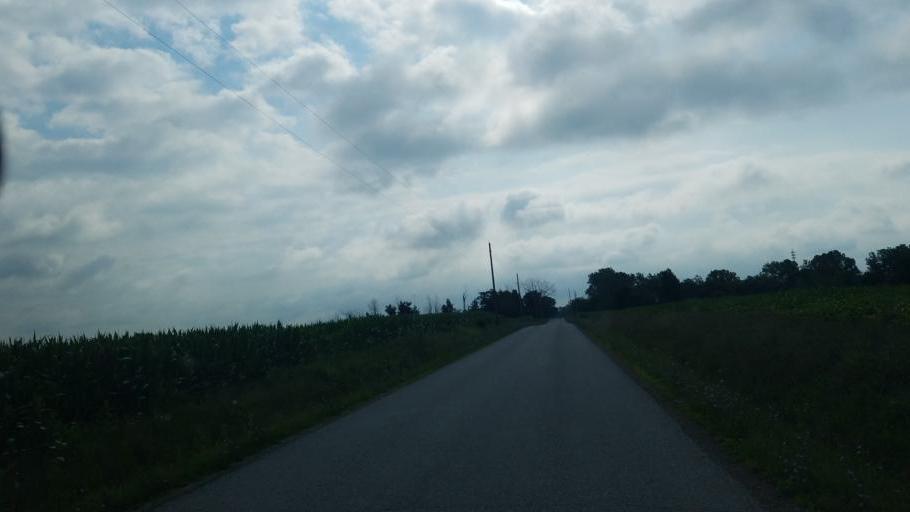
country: US
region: Ohio
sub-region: Knox County
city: Centerburg
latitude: 40.3198
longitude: -82.6893
